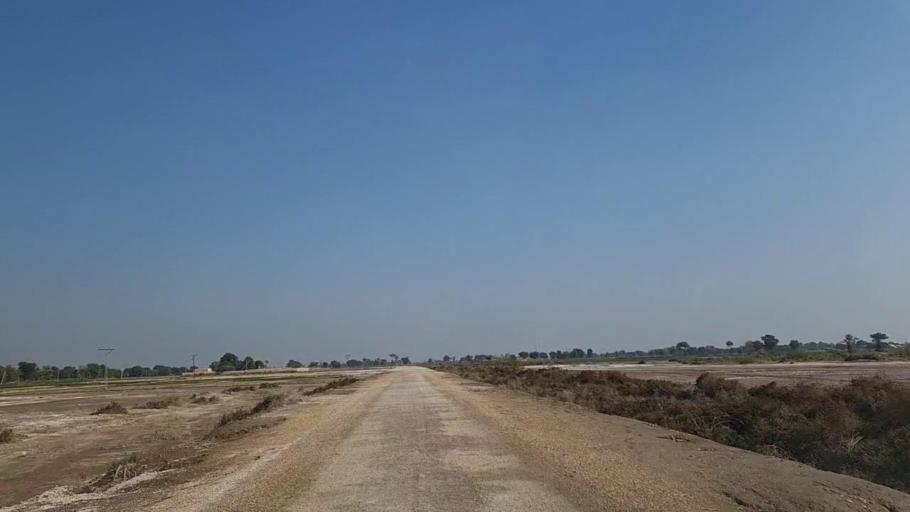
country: PK
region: Sindh
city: Daur
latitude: 26.3570
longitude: 68.3421
